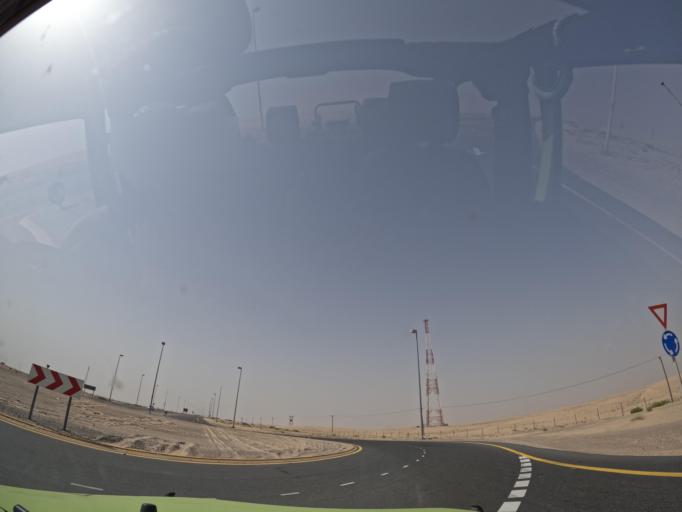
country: AE
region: Dubai
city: Dubai
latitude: 24.6902
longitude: 55.1373
